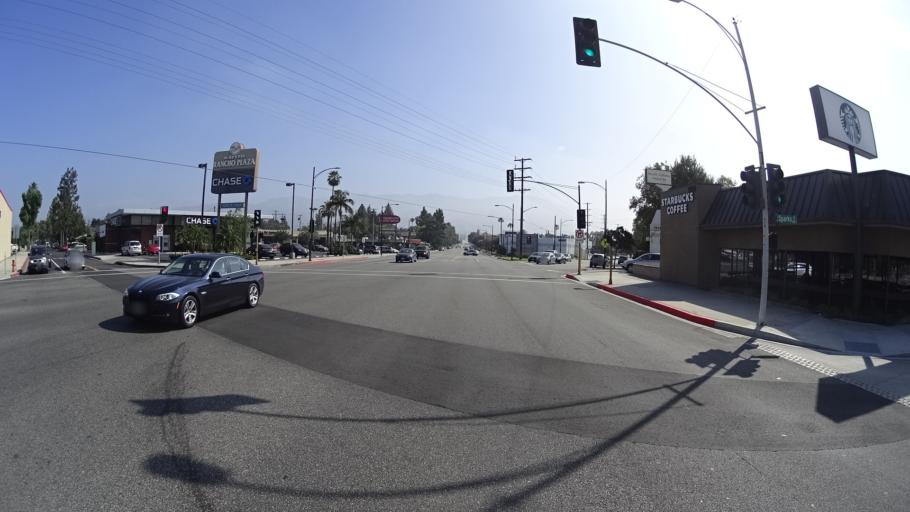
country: US
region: California
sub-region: Los Angeles County
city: Burbank
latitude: 34.1680
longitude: -118.3223
